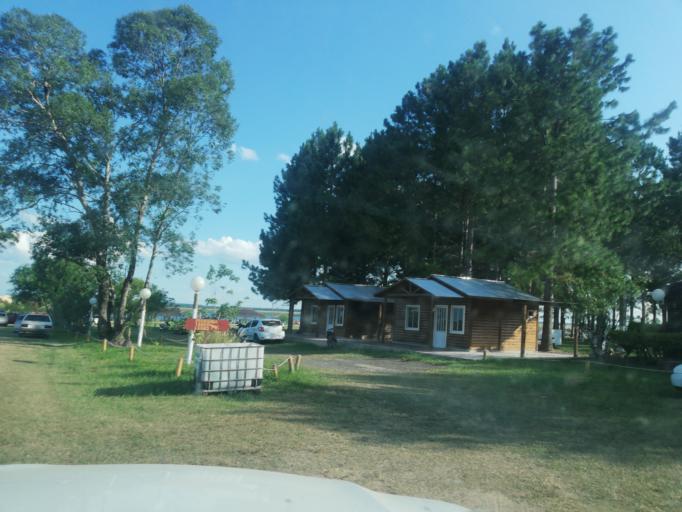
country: AR
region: Corrientes
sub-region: Departamento de San Miguel
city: San Miguel
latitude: -28.0050
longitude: -57.5938
